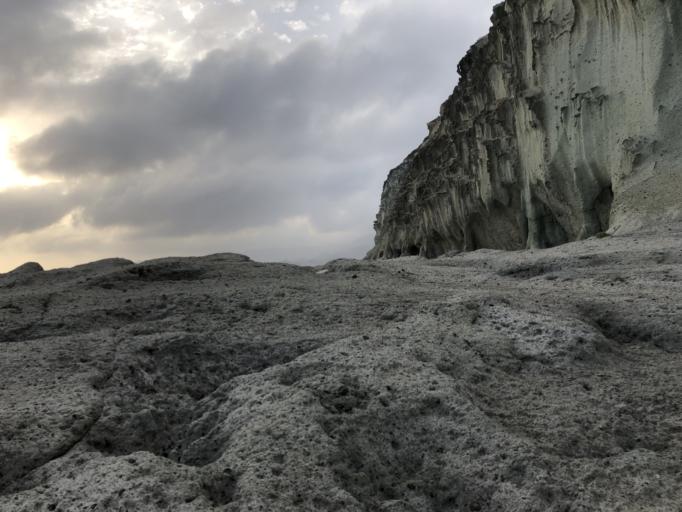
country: IT
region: Sardinia
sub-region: Provincia di Oristano
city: Bosa
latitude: 40.2990
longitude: 8.4669
